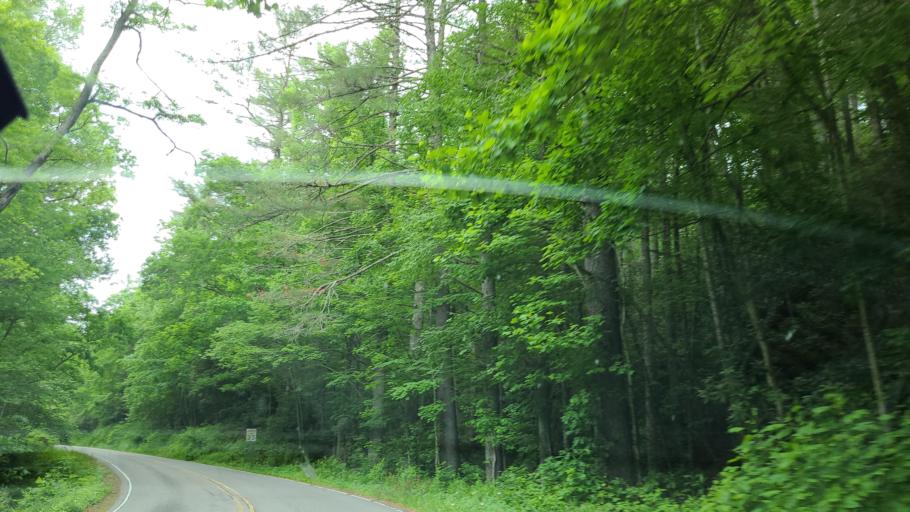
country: US
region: North Carolina
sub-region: Macon County
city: Franklin
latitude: 35.0798
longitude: -83.2578
